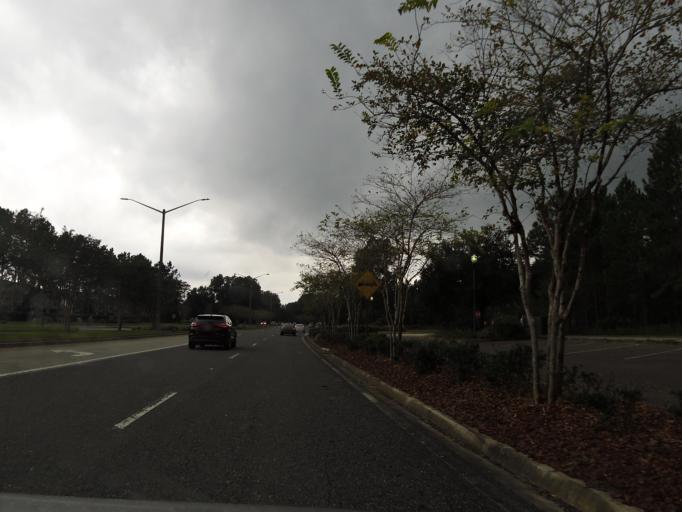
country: US
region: Florida
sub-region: Clay County
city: Lakeside
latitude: 30.1756
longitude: -81.8494
